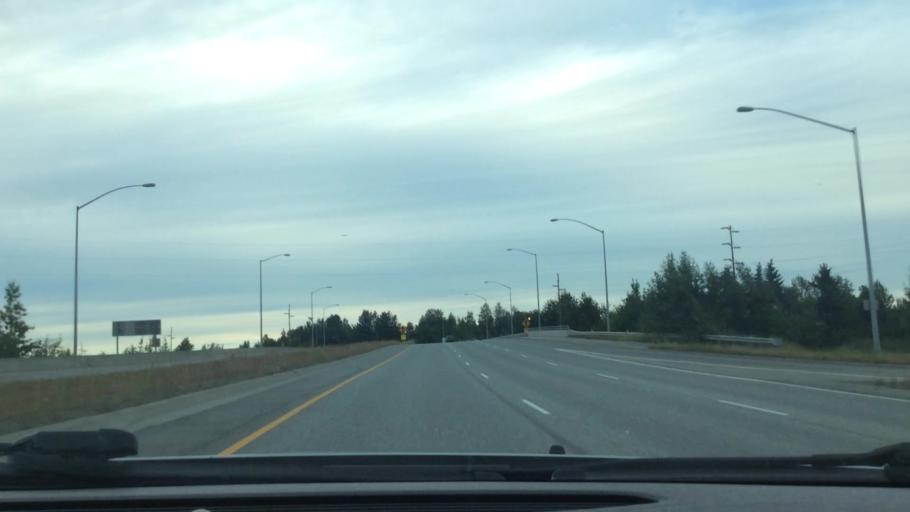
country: US
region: Alaska
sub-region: Anchorage Municipality
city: Anchorage
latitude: 61.1745
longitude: -149.9157
